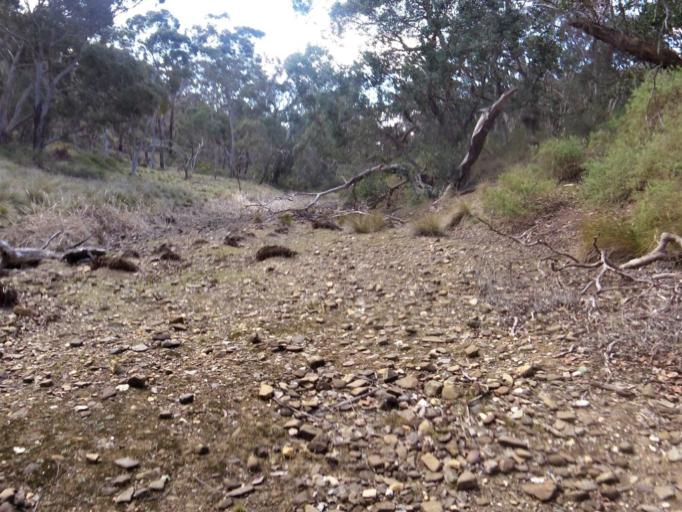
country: AU
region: Victoria
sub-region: Moorabool
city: Bacchus Marsh
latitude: -37.6610
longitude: 144.4964
